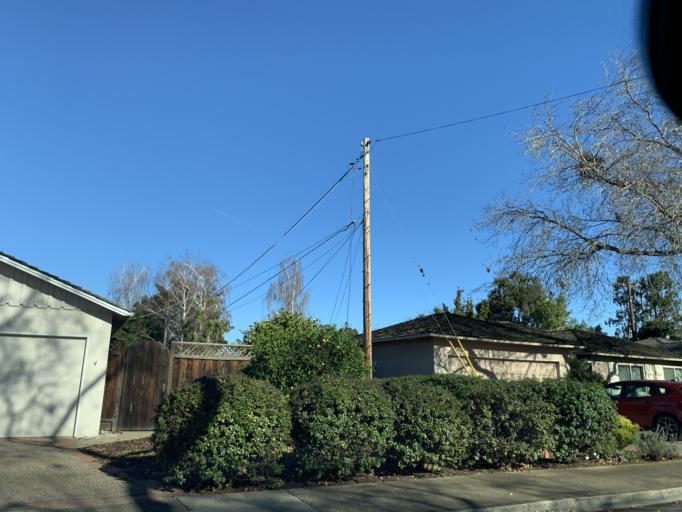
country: US
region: California
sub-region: Santa Clara County
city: Los Altos
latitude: 37.3902
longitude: -122.1019
